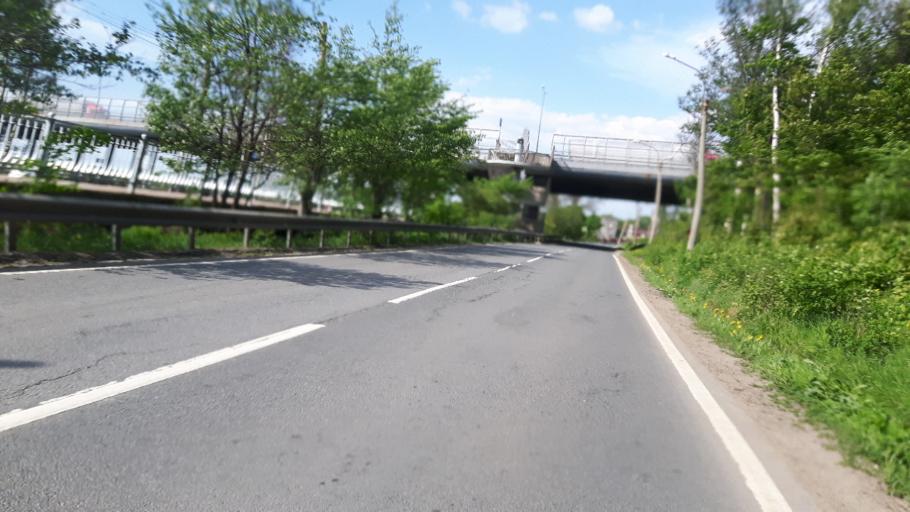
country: RU
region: Leningrad
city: Gorskaya
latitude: 60.0381
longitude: 29.9781
